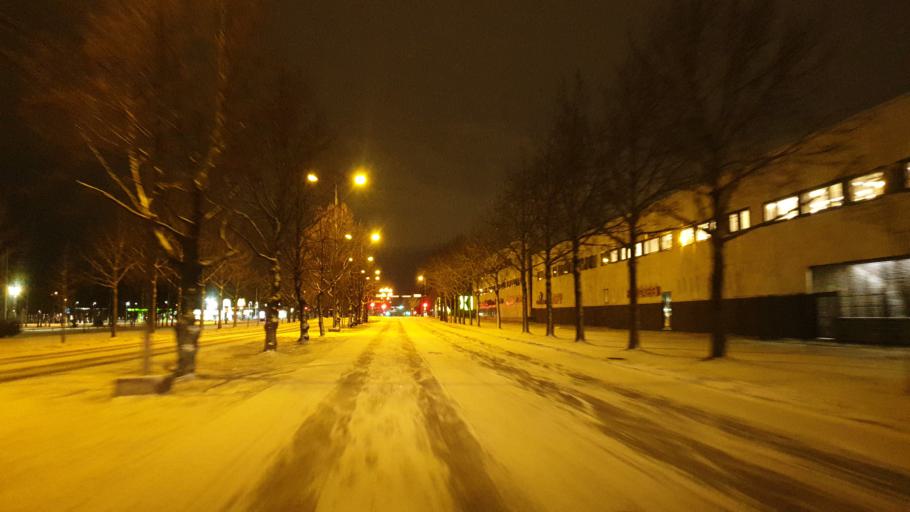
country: FI
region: Northern Ostrobothnia
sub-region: Oulu
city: Oulu
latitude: 64.9943
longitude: 25.4649
